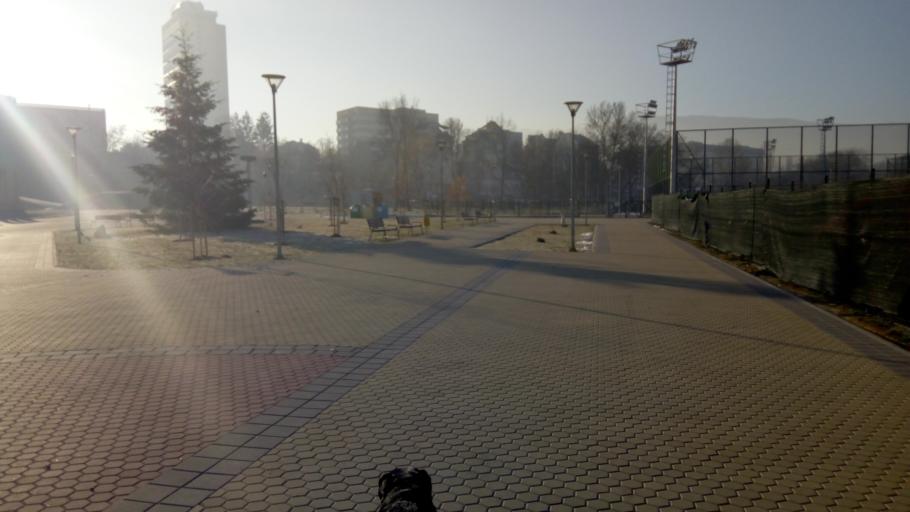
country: BG
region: Sofia-Capital
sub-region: Stolichna Obshtina
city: Sofia
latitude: 42.6953
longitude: 23.3068
